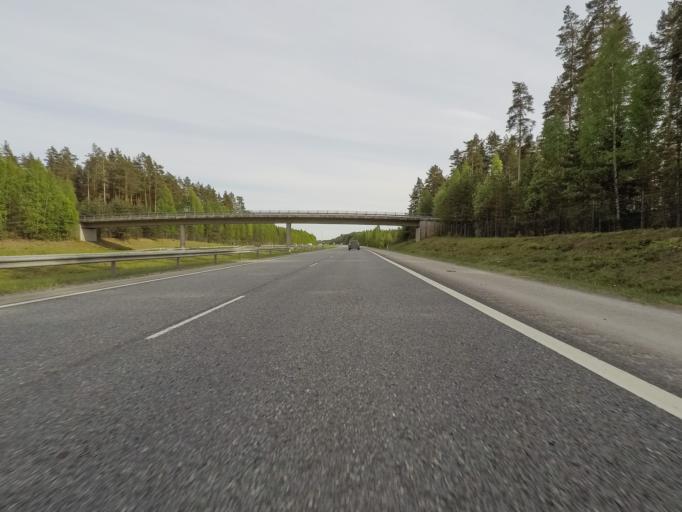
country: FI
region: Haeme
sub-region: Haemeenlinna
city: Janakkala
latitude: 60.9262
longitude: 24.5227
